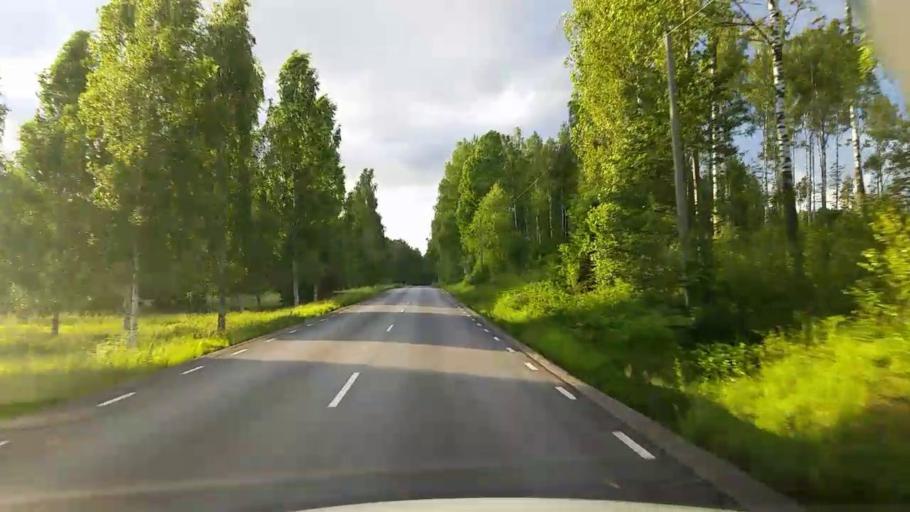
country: SE
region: Vaestmanland
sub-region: Kopings Kommun
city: Kolsva
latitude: 59.7342
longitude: 15.8257
